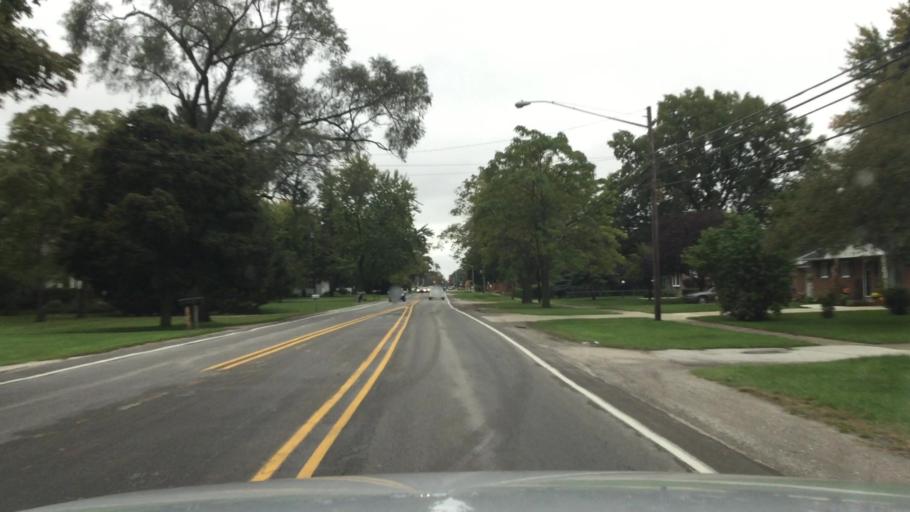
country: US
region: Michigan
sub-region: Saginaw County
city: Shields
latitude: 43.4432
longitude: -84.0050
